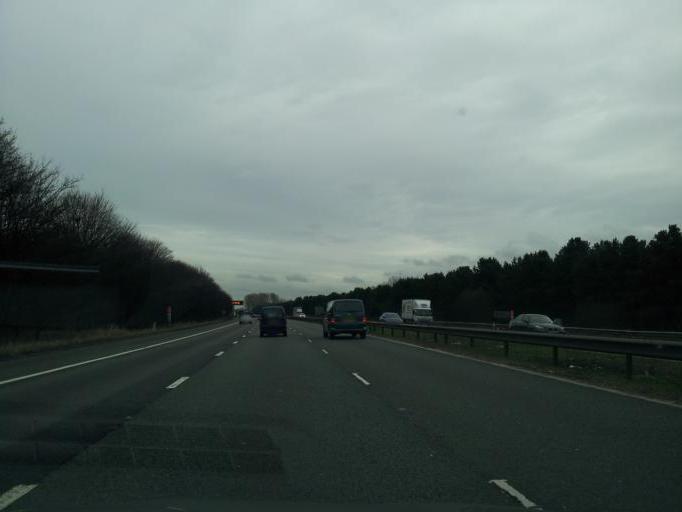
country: GB
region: England
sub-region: Warrington
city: Lymm
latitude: 53.3332
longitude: -2.4780
